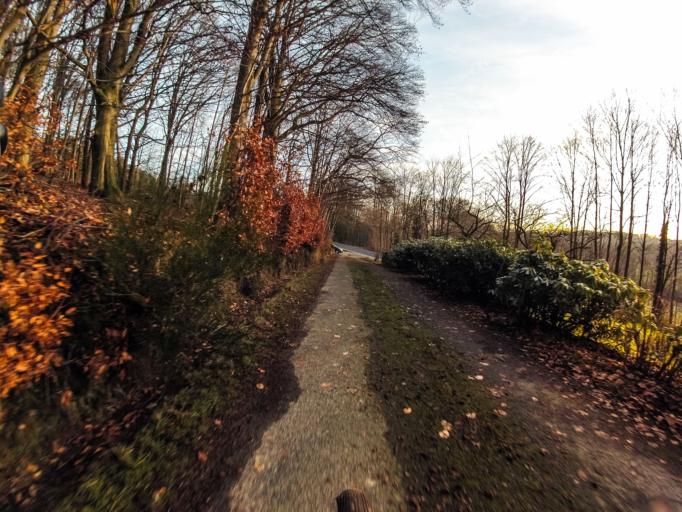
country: DE
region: North Rhine-Westphalia
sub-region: Regierungsbezirk Munster
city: Westerkappeln
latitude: 52.2896
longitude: 7.8364
